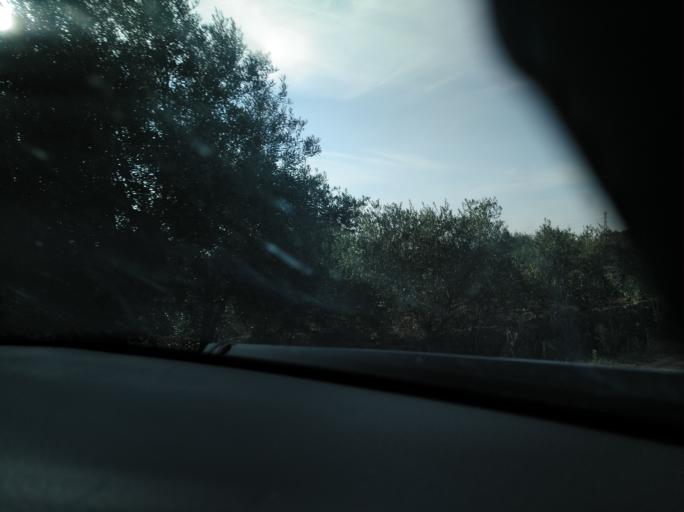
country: PT
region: Portalegre
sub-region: Elvas
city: Elvas
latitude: 38.8678
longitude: -7.2779
